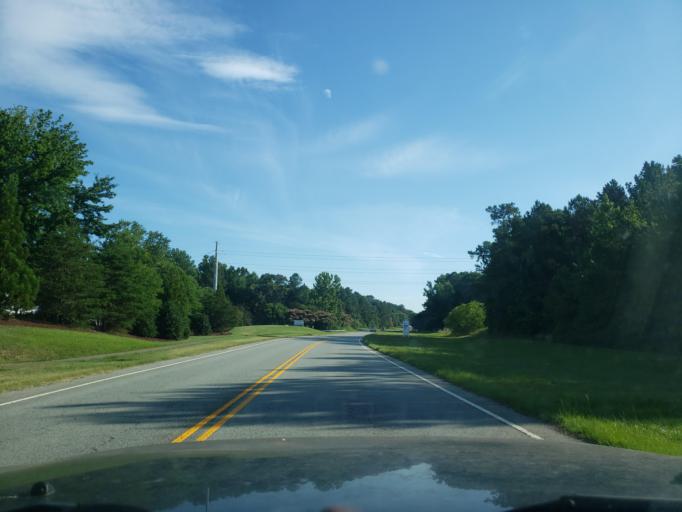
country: US
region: North Carolina
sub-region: Durham County
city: Durham
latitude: 35.9356
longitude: -78.8792
